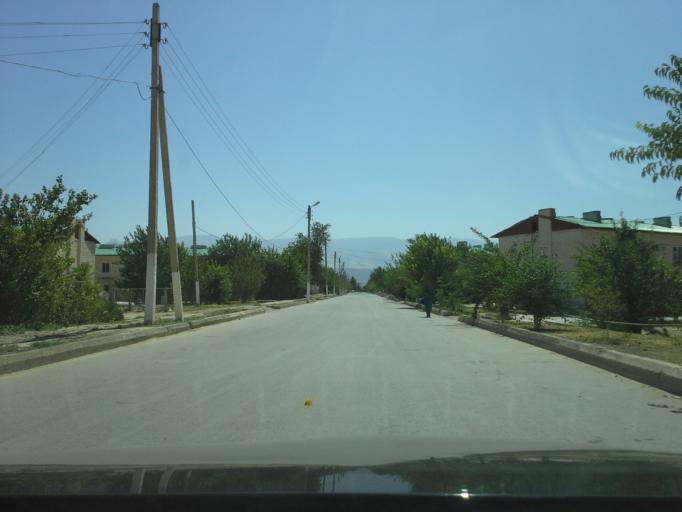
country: TM
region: Ahal
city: Ashgabat
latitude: 38.0070
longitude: 58.3040
